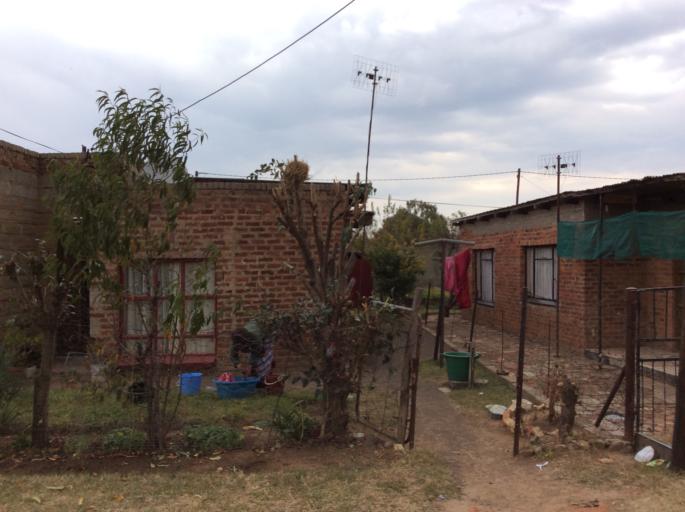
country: ZA
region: Orange Free State
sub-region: Xhariep District Municipality
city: Dewetsdorp
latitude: -29.5838
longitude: 26.6782
